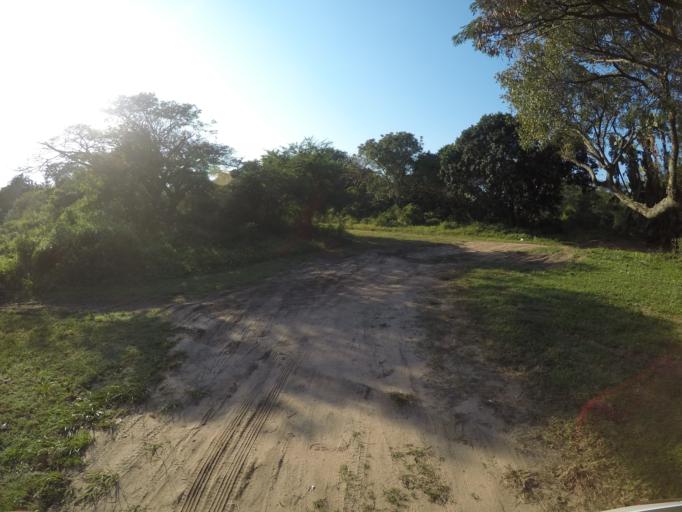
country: ZA
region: KwaZulu-Natal
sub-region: uThungulu District Municipality
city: Richards Bay
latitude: -28.7815
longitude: 32.0884
